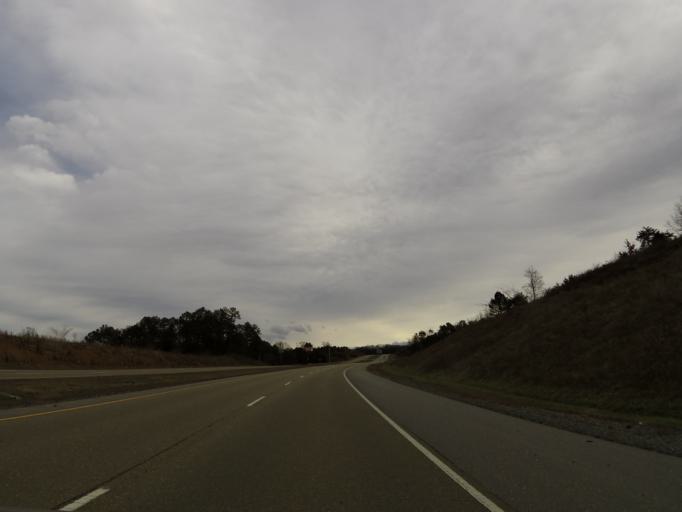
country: US
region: Tennessee
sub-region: Cocke County
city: Newport
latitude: 36.0049
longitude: -83.0853
